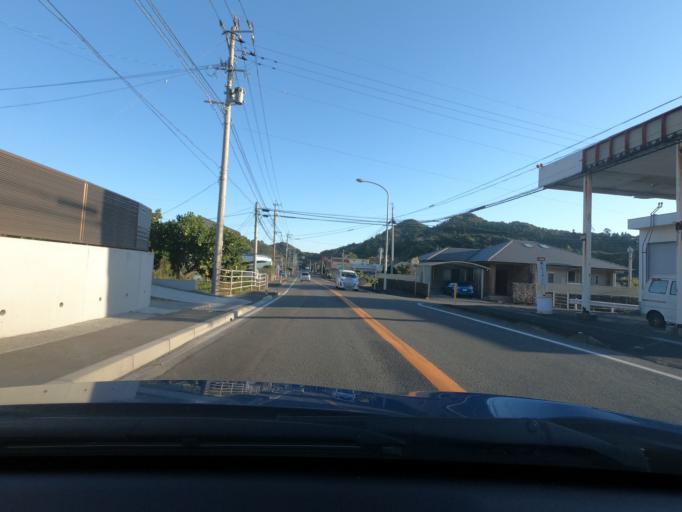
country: JP
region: Kagoshima
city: Satsumasendai
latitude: 31.8561
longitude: 130.2331
